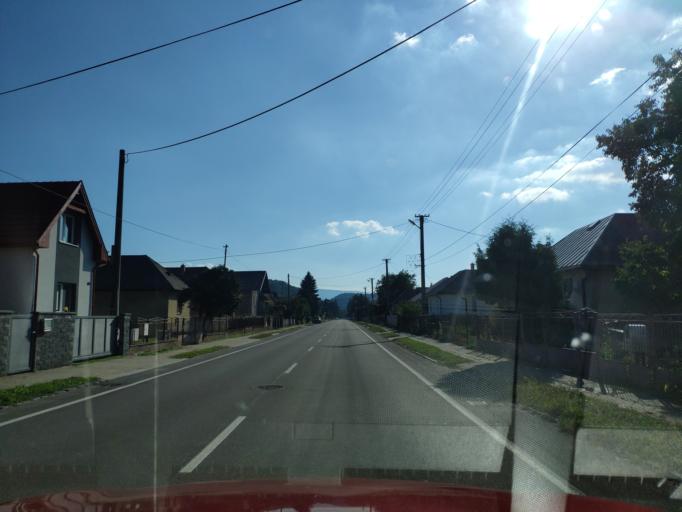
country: SK
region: Presovsky
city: Snina
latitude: 49.0060
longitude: 22.2370
